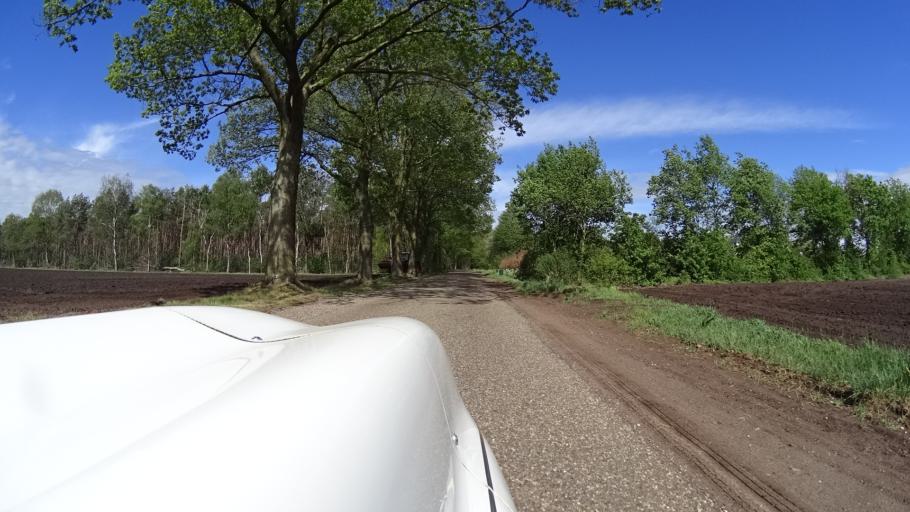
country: NL
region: North Brabant
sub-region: Gemeente Mill en Sint Hubert
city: Wilbertoord
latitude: 51.5955
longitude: 5.8114
